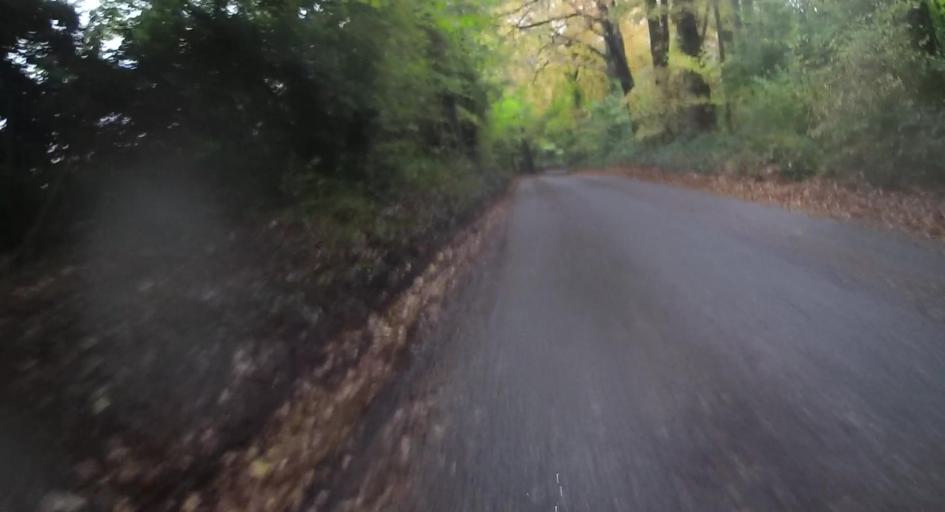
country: GB
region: England
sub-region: Hampshire
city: Four Marks
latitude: 51.1361
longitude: -1.0325
